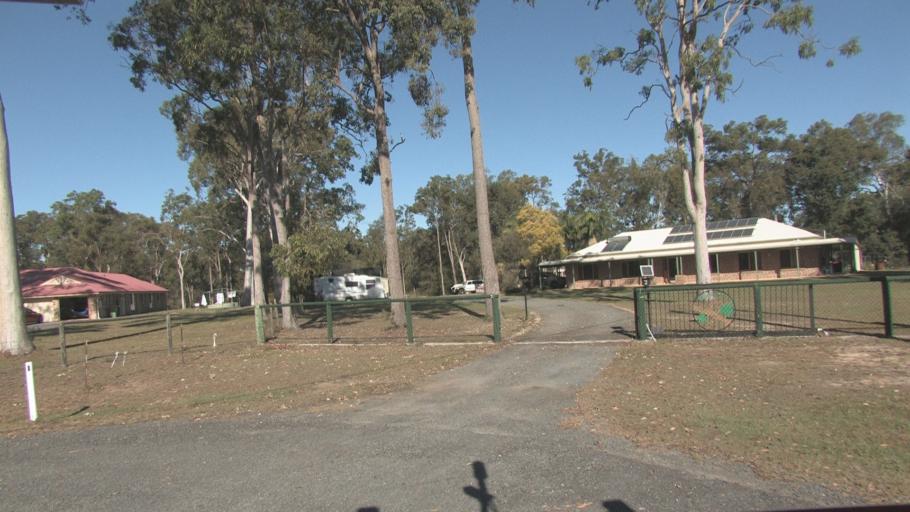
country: AU
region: Queensland
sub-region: Logan
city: Chambers Flat
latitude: -27.7387
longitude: 153.0749
